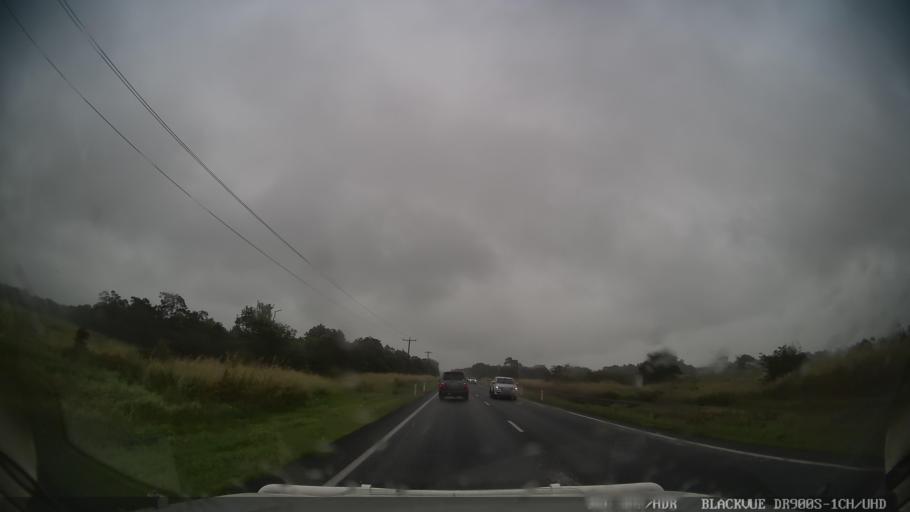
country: AU
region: Queensland
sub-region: Cassowary Coast
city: Innisfail
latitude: -17.6536
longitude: 146.0349
